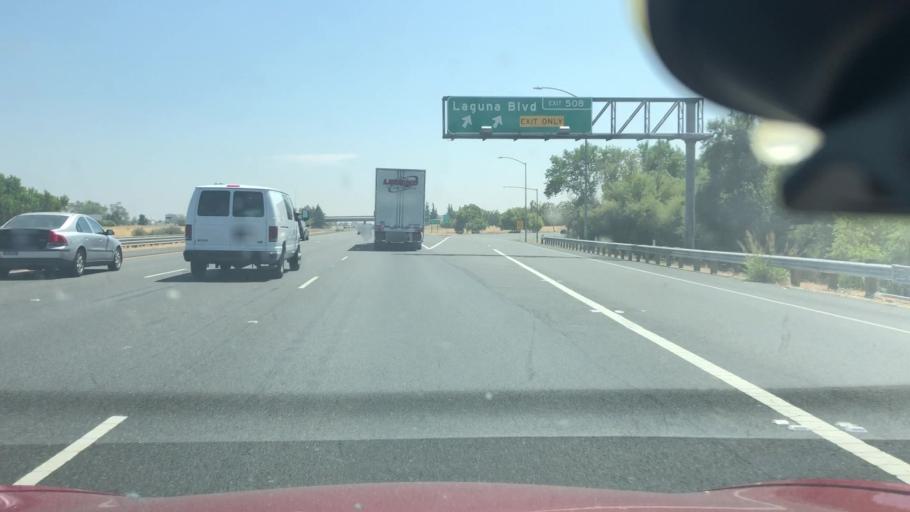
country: US
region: California
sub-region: Sacramento County
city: Laguna
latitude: 38.4316
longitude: -121.4886
